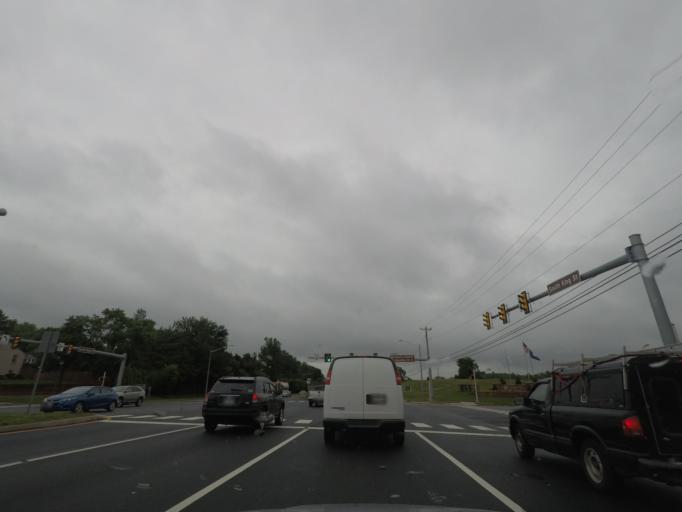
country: US
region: Virginia
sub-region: Loudoun County
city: Leesburg
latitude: 39.0966
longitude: -77.5795
